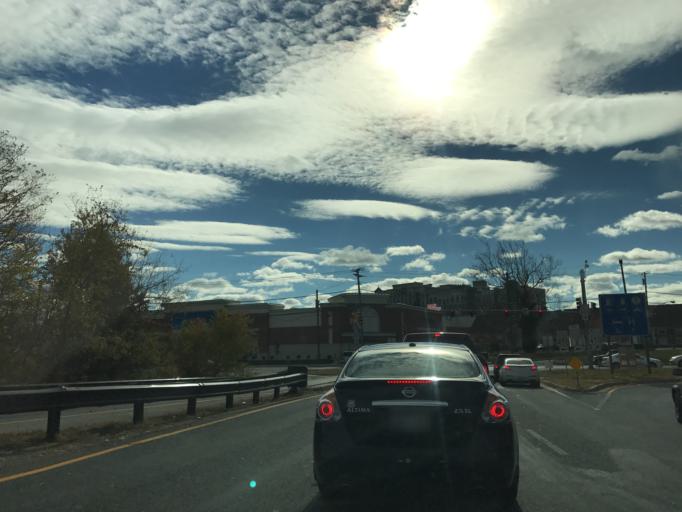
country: US
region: Maryland
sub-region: Anne Arundel County
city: Parole
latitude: 38.9845
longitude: -76.5405
